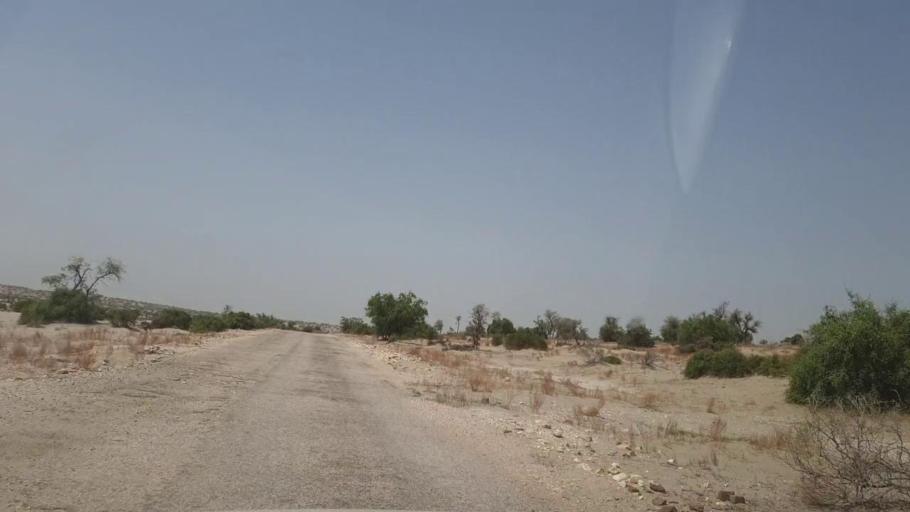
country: PK
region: Sindh
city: Khanpur
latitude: 27.3427
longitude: 69.3169
